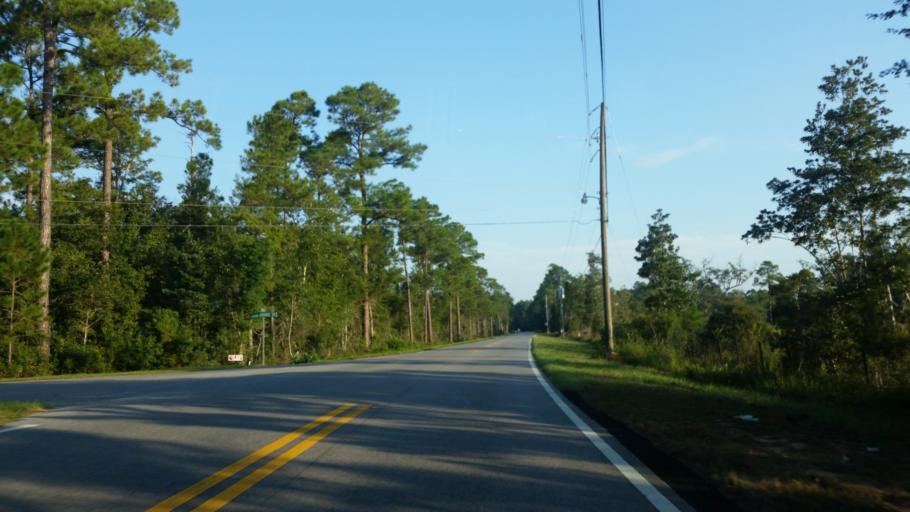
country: US
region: Florida
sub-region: Santa Rosa County
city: East Milton
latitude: 30.5990
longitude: -87.0068
